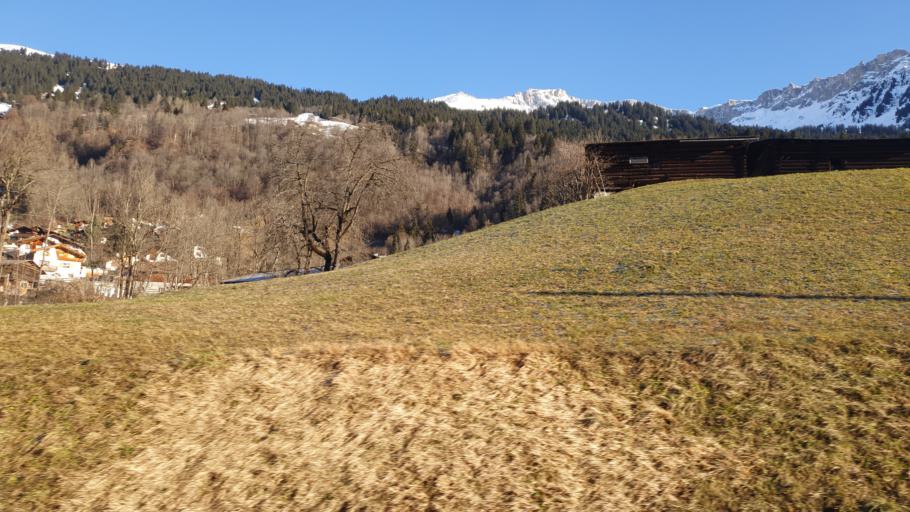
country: CH
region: Grisons
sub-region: Praettigau/Davos District
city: Klosters Serneus
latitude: 46.9067
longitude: 9.8120
